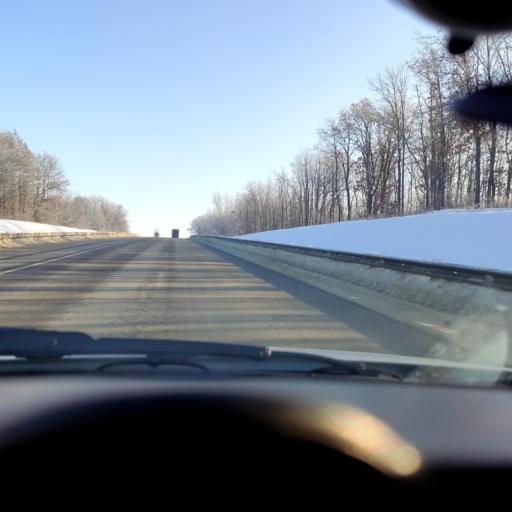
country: RU
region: Kursk
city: Tim
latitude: 51.6514
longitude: 37.0033
